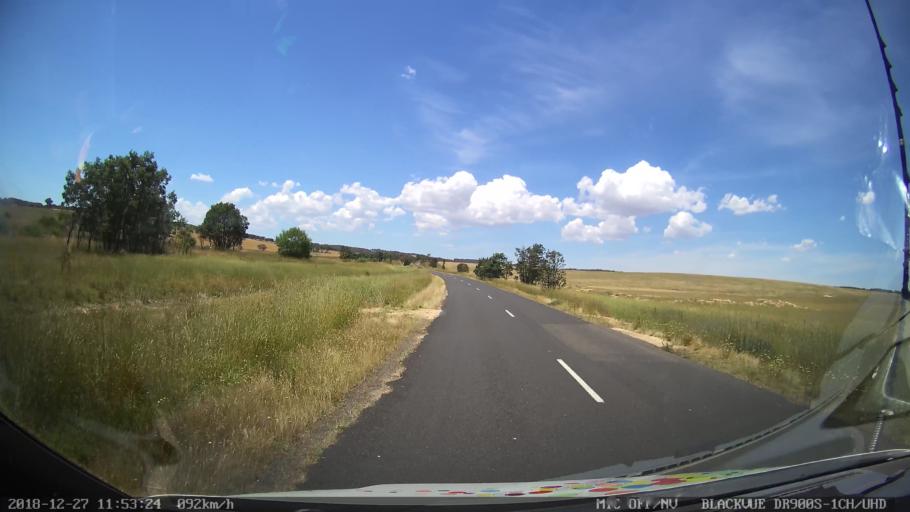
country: AU
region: New South Wales
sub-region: Blayney
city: Blayney
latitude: -33.6613
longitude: 149.4014
